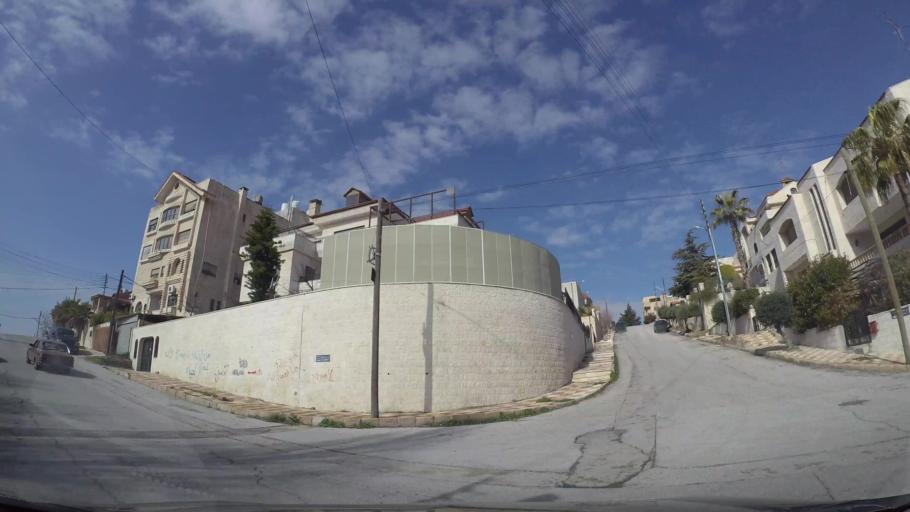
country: JO
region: Amman
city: Al Jubayhah
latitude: 31.9998
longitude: 35.8916
